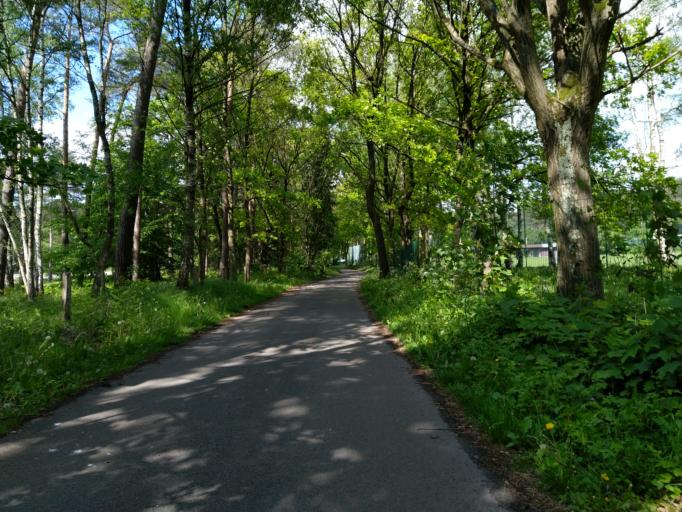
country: BE
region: Wallonia
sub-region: Province du Hainaut
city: Jurbise
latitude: 50.5025
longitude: 3.9268
